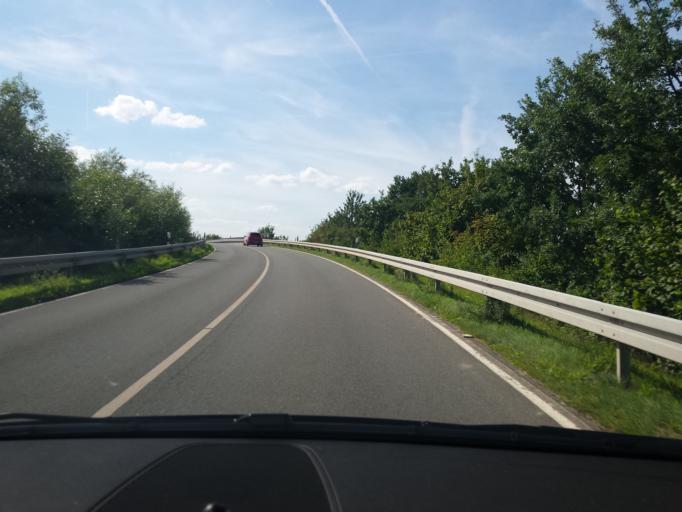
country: DE
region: North Rhine-Westphalia
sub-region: Regierungsbezirk Arnsberg
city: Lippstadt
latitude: 51.6543
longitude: 8.2928
